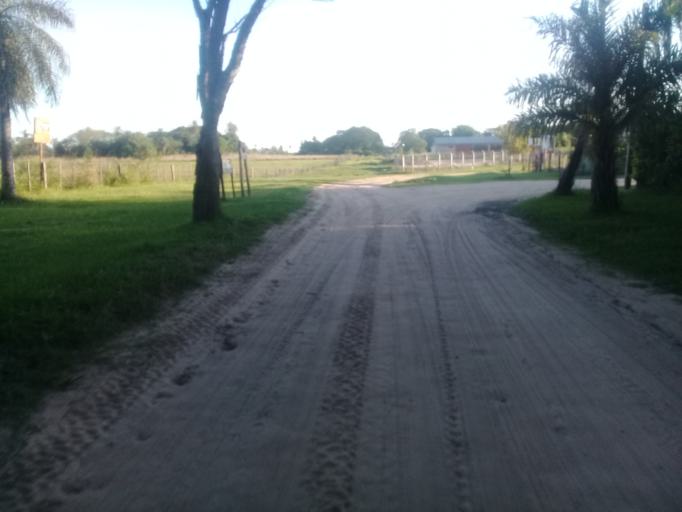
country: AR
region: Corrientes
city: San Luis del Palmar
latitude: -27.4664
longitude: -58.6623
